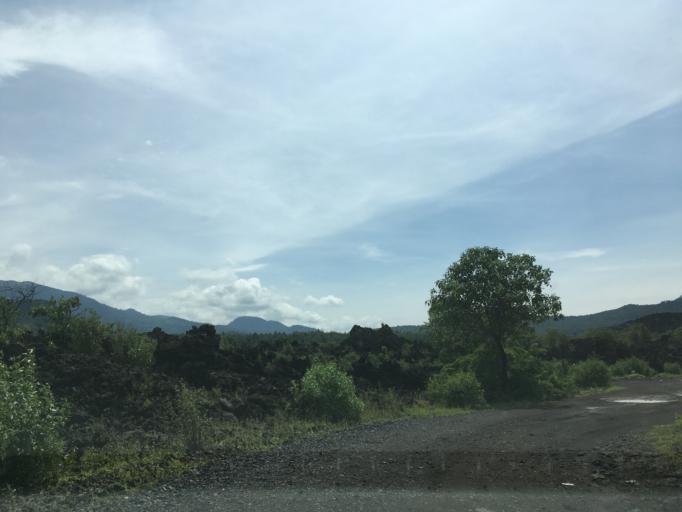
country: MX
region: Michoacan
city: Angahuan
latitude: 19.5280
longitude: -102.2401
